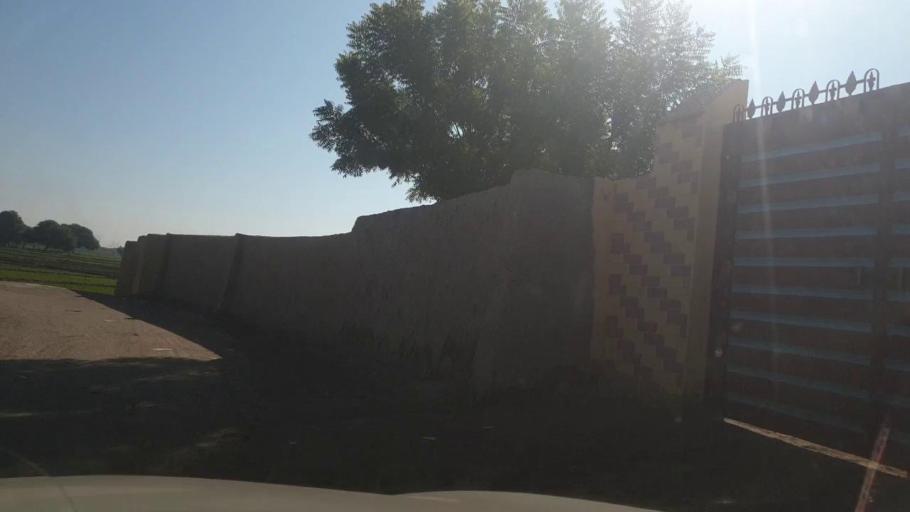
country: PK
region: Sindh
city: Bhan
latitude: 26.5445
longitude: 67.6626
